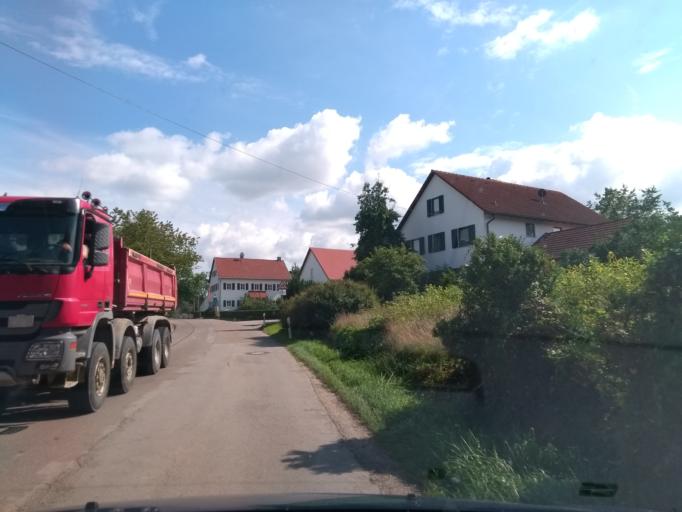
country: DE
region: Bavaria
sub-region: Upper Bavaria
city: Schwabhausen
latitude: 48.3831
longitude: 11.3482
